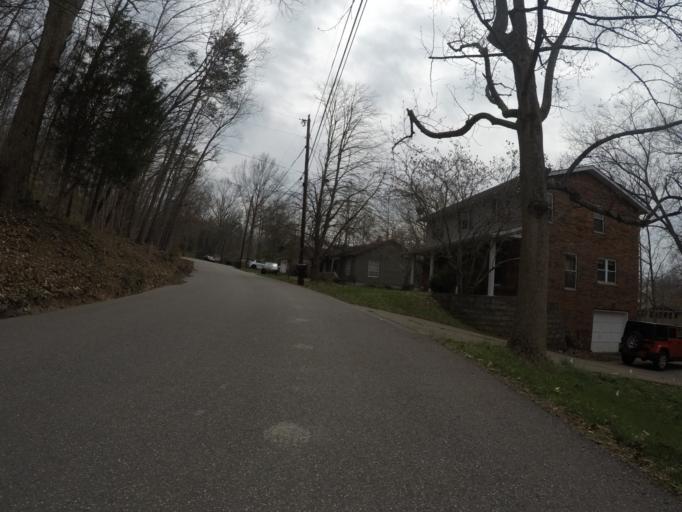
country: US
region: West Virginia
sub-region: Cabell County
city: Pea Ridge
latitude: 38.4193
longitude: -82.3247
